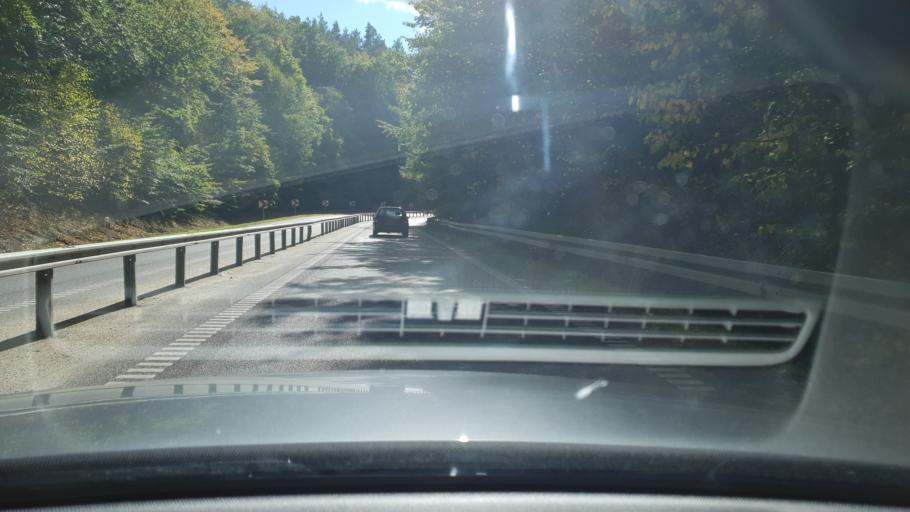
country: PL
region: Pomeranian Voivodeship
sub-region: Powiat wejherowski
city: Rekowo Dolne
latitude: 54.6285
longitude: 18.3439
